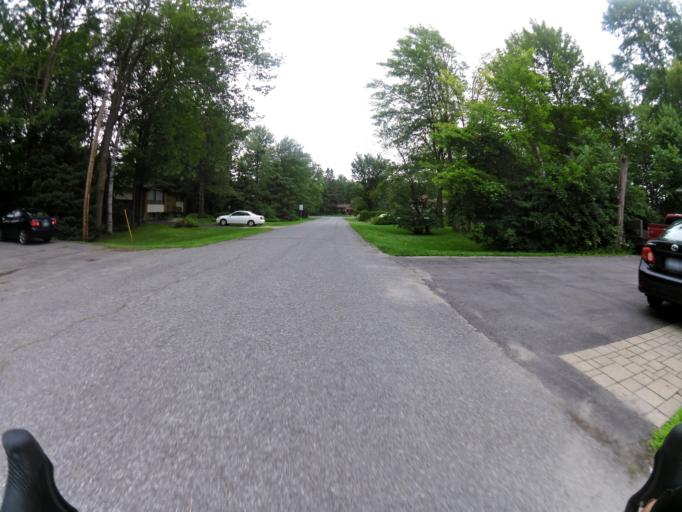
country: CA
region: Ontario
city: Ottawa
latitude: 45.3269
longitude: -75.7065
